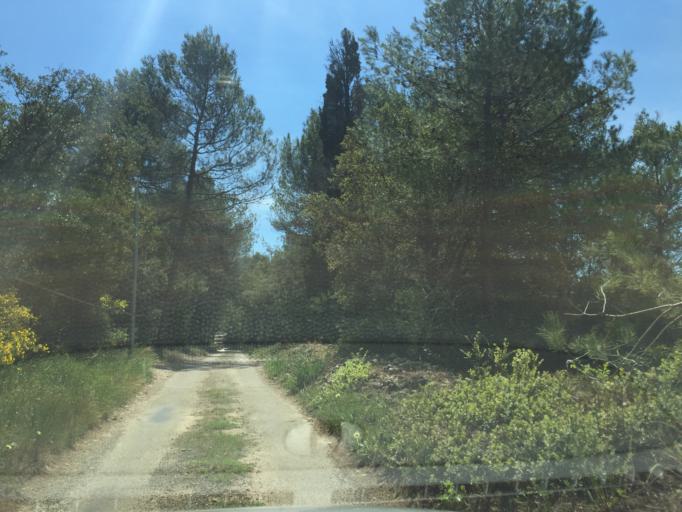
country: FR
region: Provence-Alpes-Cote d'Azur
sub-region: Departement du Var
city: Lorgues
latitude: 43.4733
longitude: 6.3705
